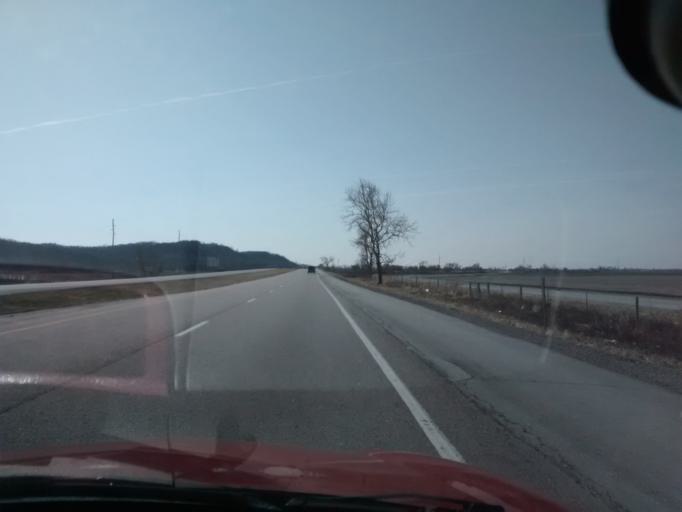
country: US
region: Iowa
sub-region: Pottawattamie County
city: Carter Lake
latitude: 41.3408
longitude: -95.8911
